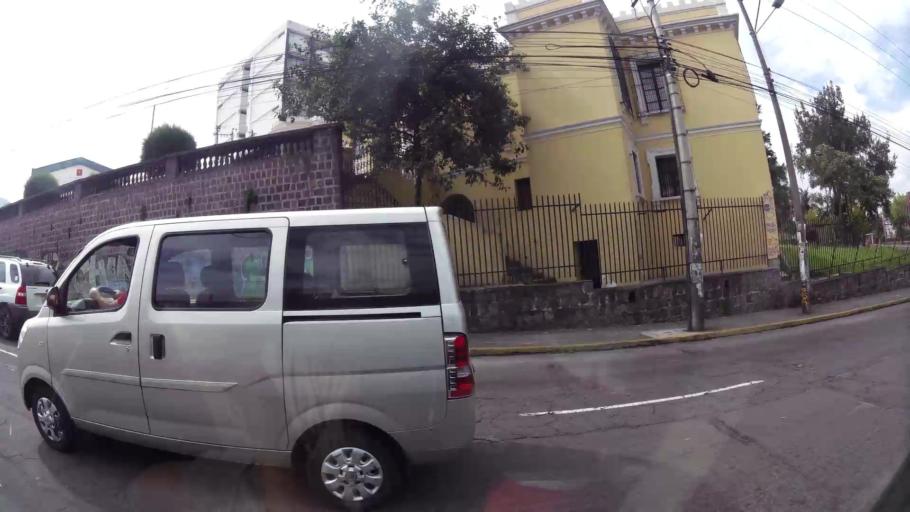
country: EC
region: Pichincha
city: Quito
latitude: -0.2125
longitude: -78.4914
